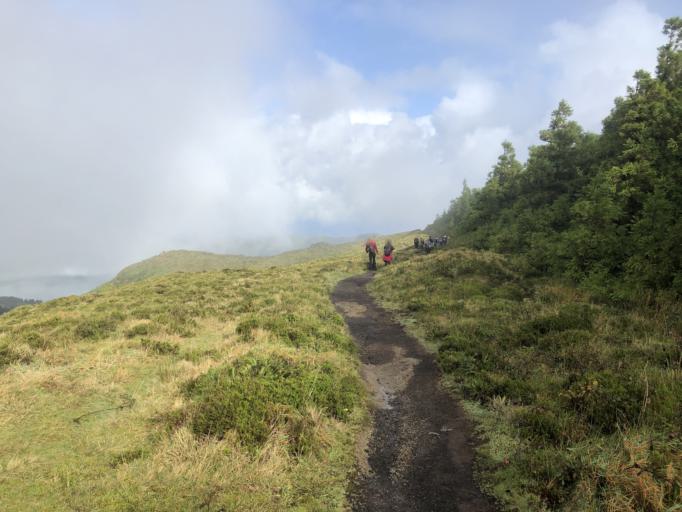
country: PT
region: Azores
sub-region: Ponta Delgada
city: Arrifes
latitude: 37.8411
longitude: -25.7628
